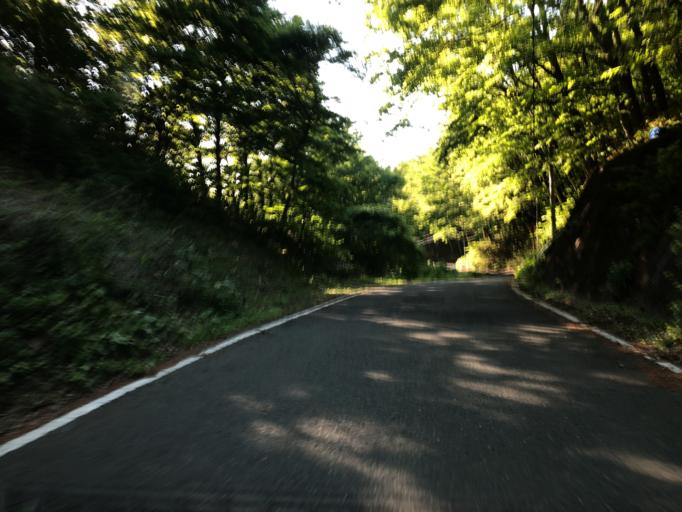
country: JP
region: Ibaraki
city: Kitaibaraki
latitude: 36.9028
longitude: 140.5932
